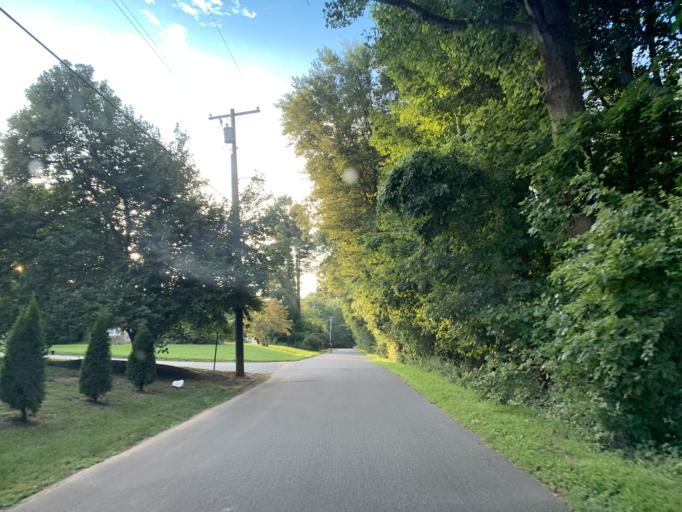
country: US
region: Maryland
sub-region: Harford County
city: Aberdeen
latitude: 39.5209
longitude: -76.1570
